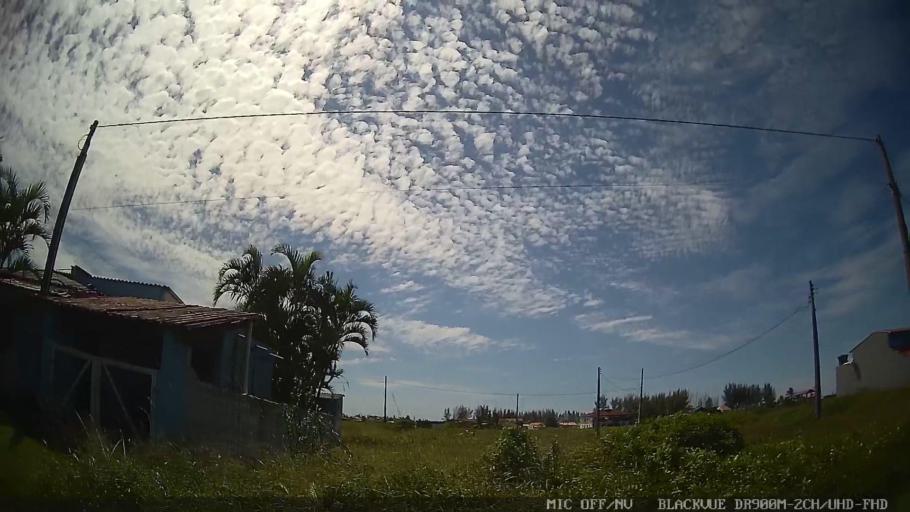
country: BR
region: Sao Paulo
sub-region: Iguape
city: Iguape
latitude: -24.7985
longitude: -47.6310
